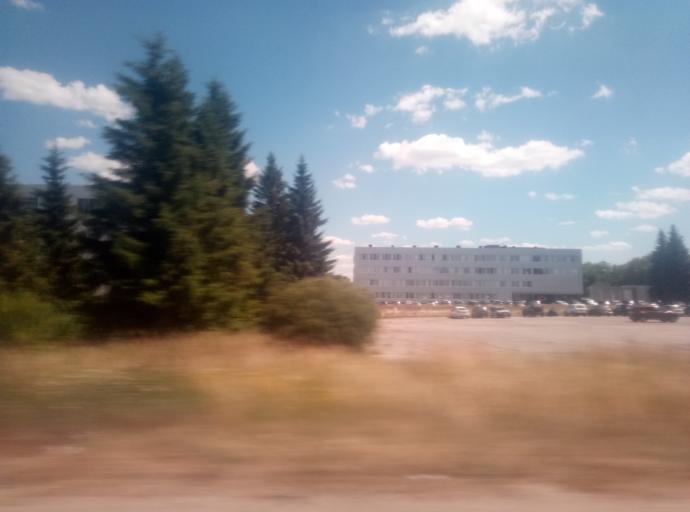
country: RU
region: Tula
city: Kireyevsk
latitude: 53.9578
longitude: 37.9383
